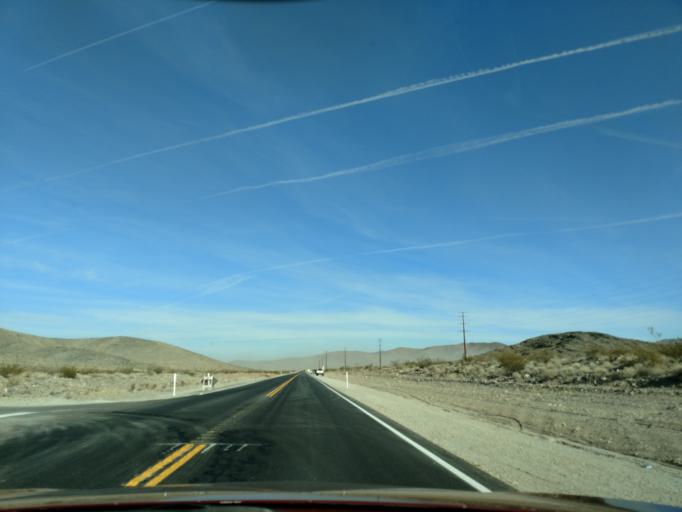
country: US
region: Nevada
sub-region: Nye County
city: Pahrump
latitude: 36.4198
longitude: -116.0700
